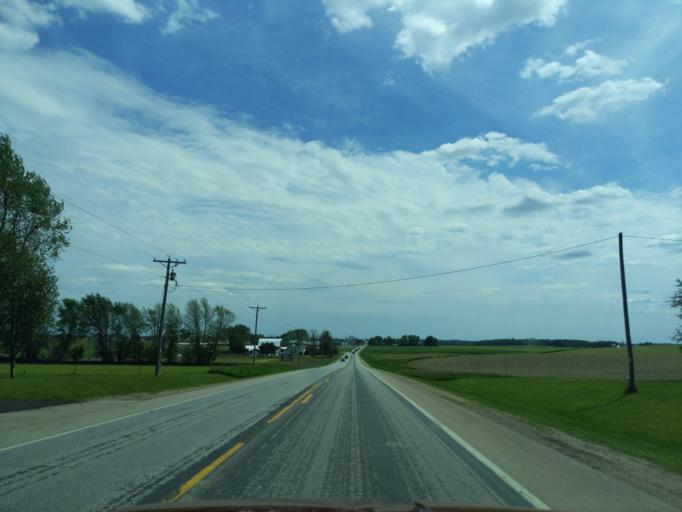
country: US
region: Wisconsin
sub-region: Dane County
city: De Forest
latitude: 43.3005
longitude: -89.3249
